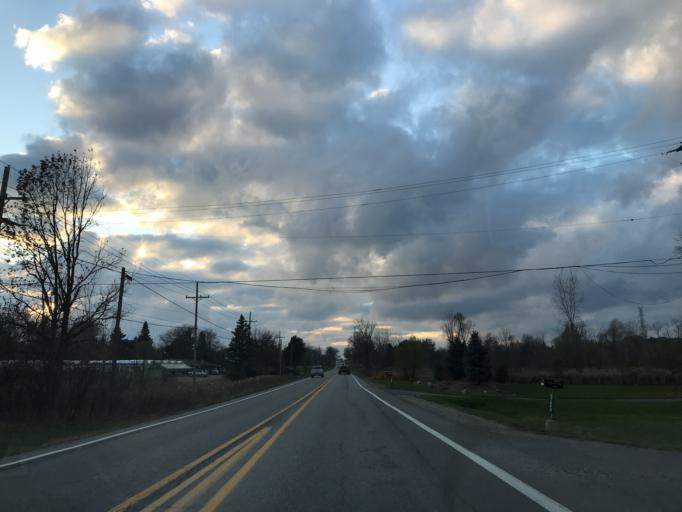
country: US
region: Michigan
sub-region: Oakland County
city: South Lyon
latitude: 42.4619
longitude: -83.6165
